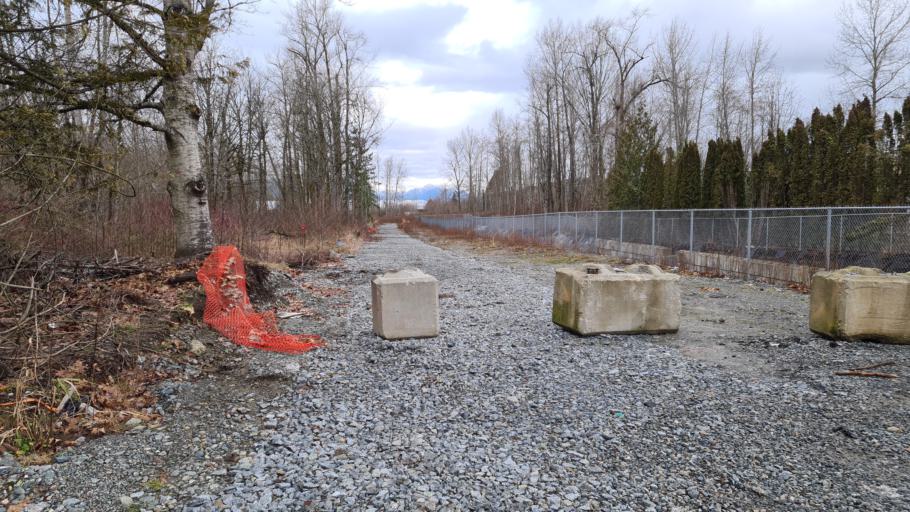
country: CA
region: British Columbia
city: Walnut Grove
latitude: 49.1445
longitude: -122.6512
